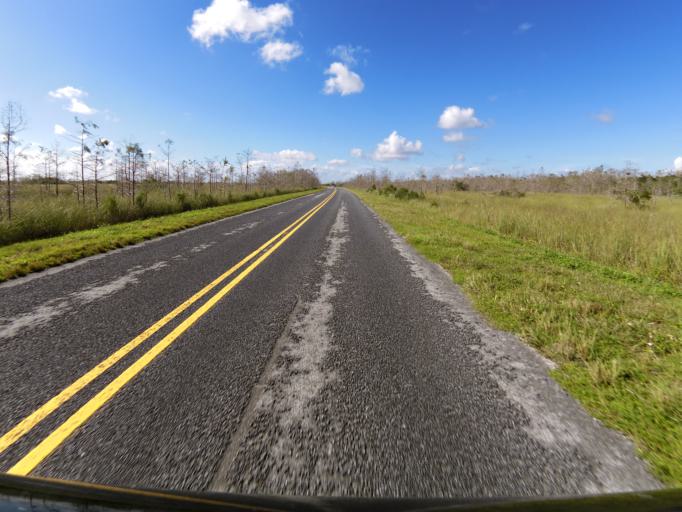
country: US
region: Florida
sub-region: Miami-Dade County
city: Florida City
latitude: 25.4336
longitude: -80.7503
